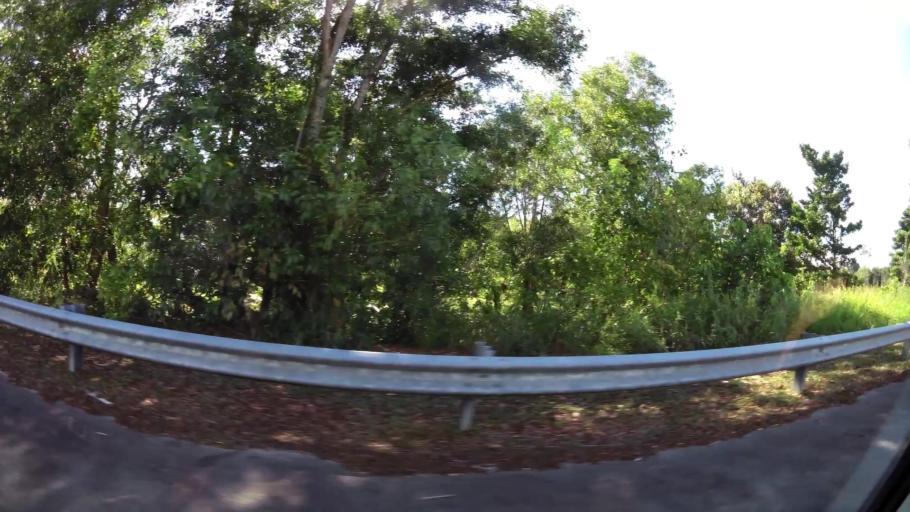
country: BN
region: Brunei and Muara
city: Bandar Seri Begawan
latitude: 4.9673
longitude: 114.9261
